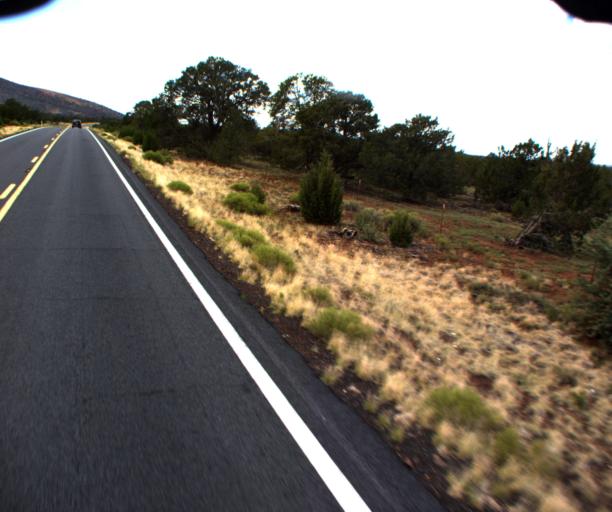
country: US
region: Arizona
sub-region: Coconino County
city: Parks
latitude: 35.5639
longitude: -111.9036
